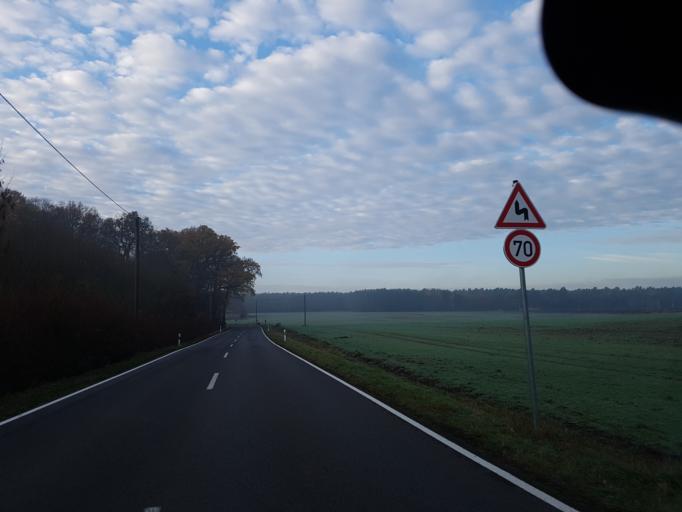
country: DE
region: Saxony-Anhalt
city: Zahna
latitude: 51.9074
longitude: 12.7721
